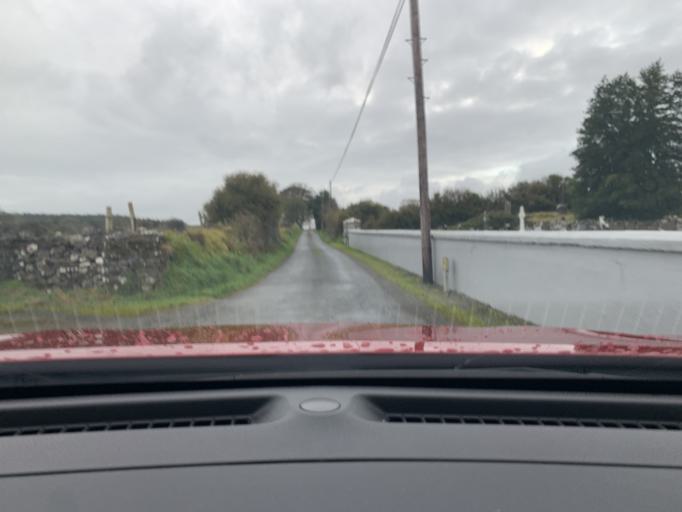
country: IE
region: Connaught
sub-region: Roscommon
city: Ballaghaderreen
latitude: 53.9669
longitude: -8.5721
